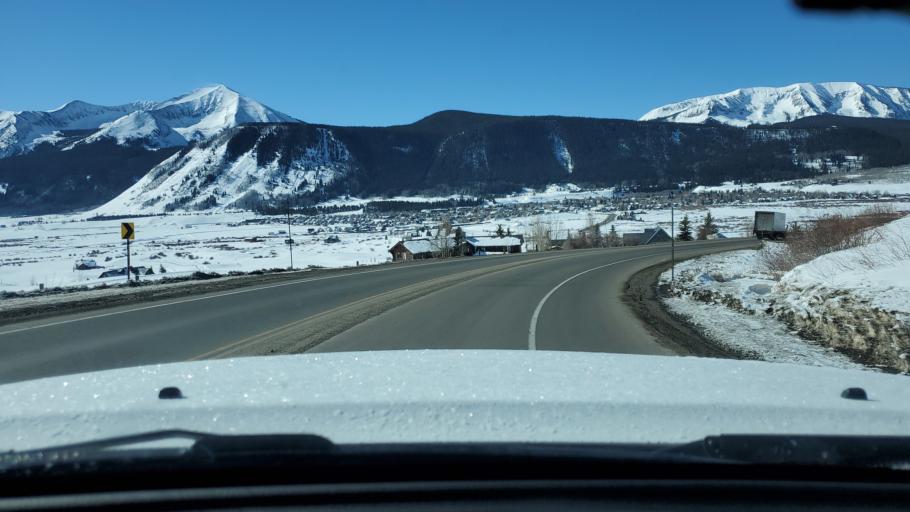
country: US
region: Colorado
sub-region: Gunnison County
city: Crested Butte
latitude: 38.8843
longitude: -106.9712
